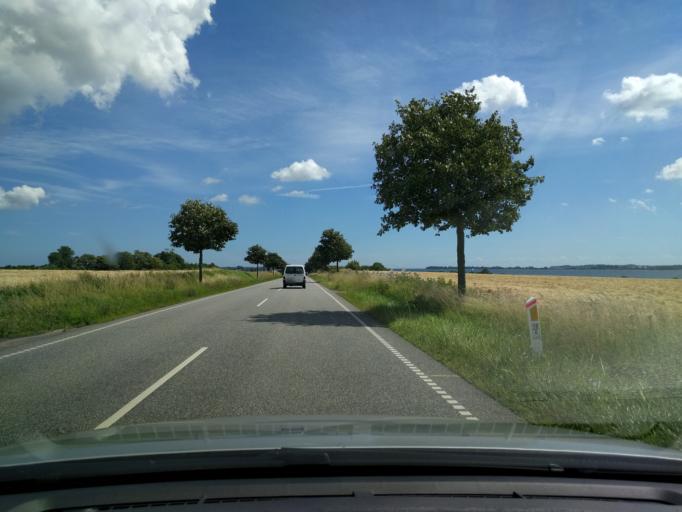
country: DK
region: Zealand
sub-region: Guldborgsund Kommune
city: Stubbekobing
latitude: 54.9121
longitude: 12.0645
